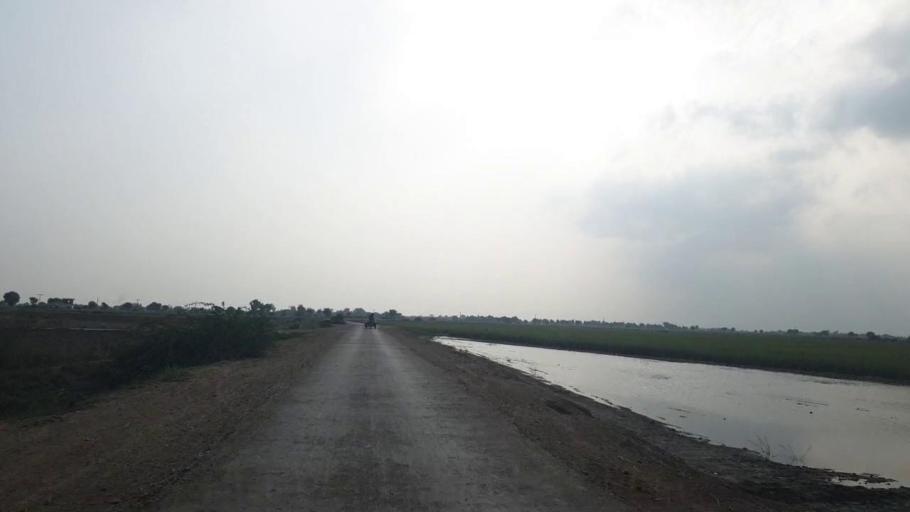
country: PK
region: Sindh
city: Badin
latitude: 24.6475
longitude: 68.6984
